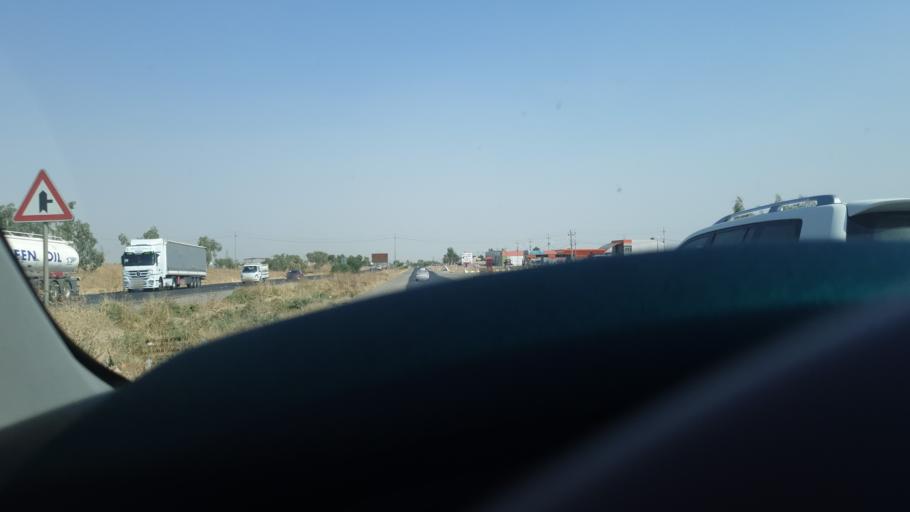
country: IQ
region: Arbil
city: Erbil
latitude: 36.2048
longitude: 43.8747
